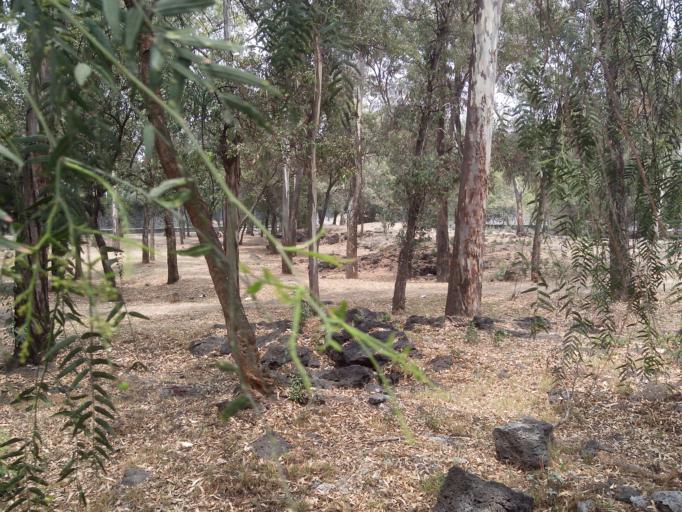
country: MX
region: Mexico City
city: Magdalena Contreras
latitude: 19.3251
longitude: -99.1878
